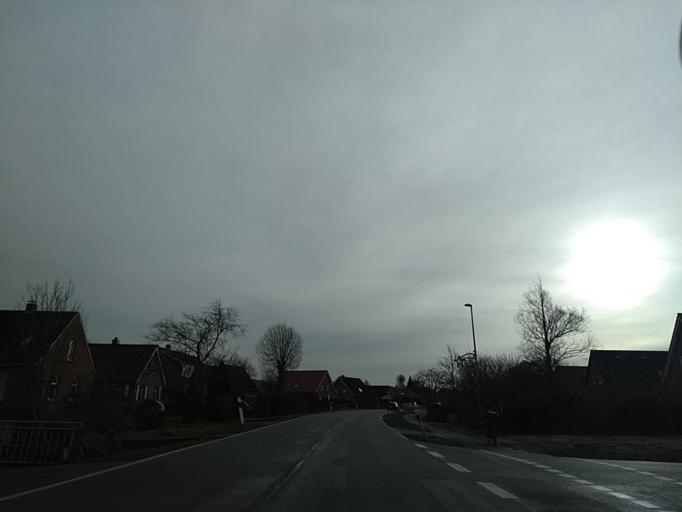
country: DE
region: Lower Saxony
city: Jemgum
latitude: 53.2748
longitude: 7.3853
